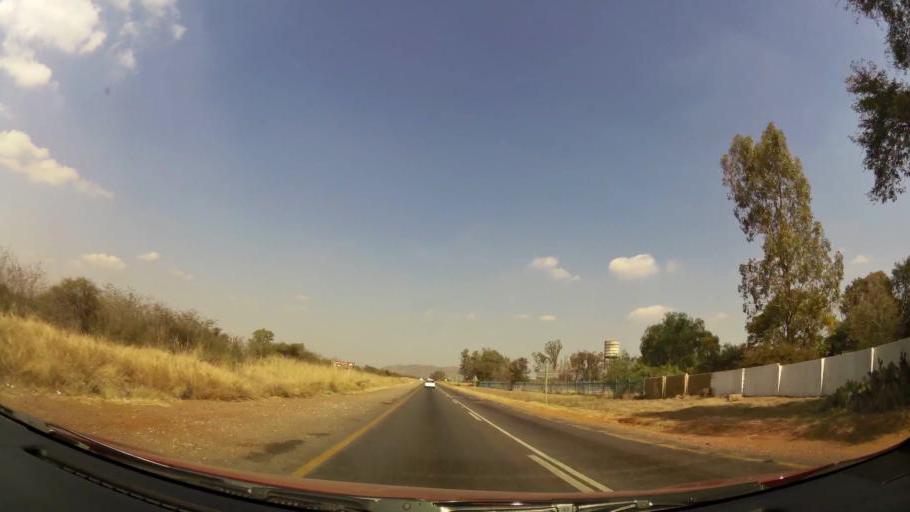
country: ZA
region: North-West
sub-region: Bojanala Platinum District Municipality
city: Rustenburg
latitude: -25.5072
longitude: 27.0990
